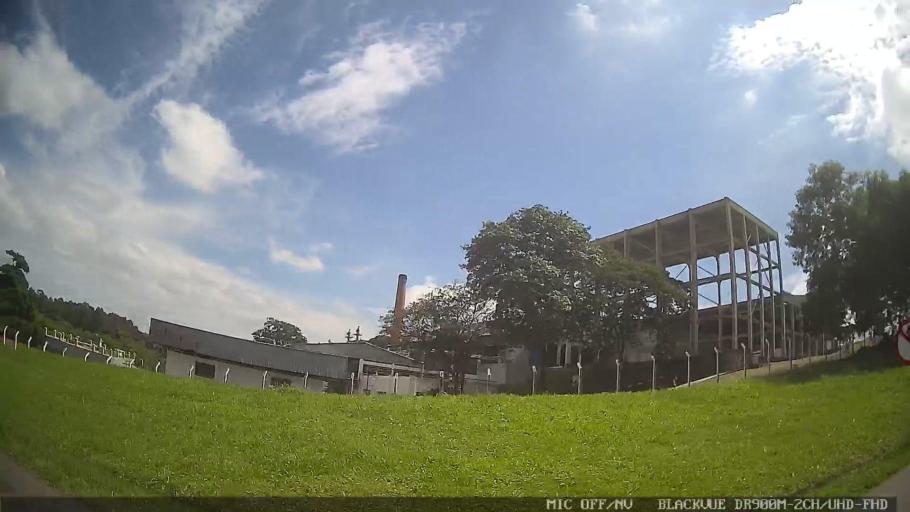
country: BR
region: Sao Paulo
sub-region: Tiete
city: Tiete
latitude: -23.1185
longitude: -47.7222
